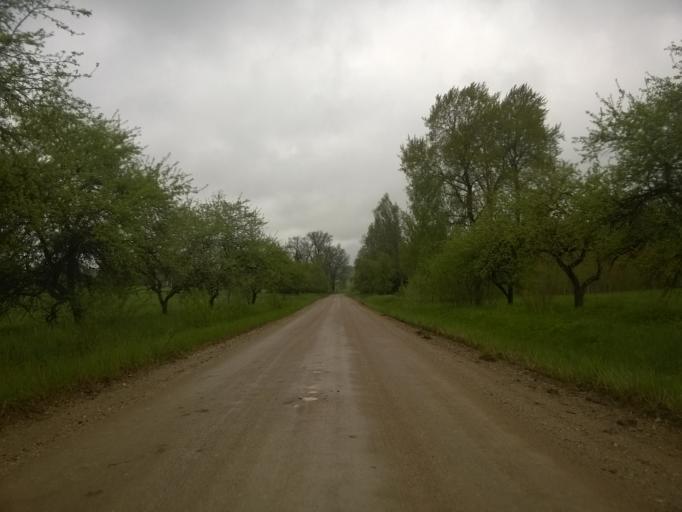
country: LV
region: Amatas Novads
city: Drabesi
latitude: 57.2202
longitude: 25.1965
